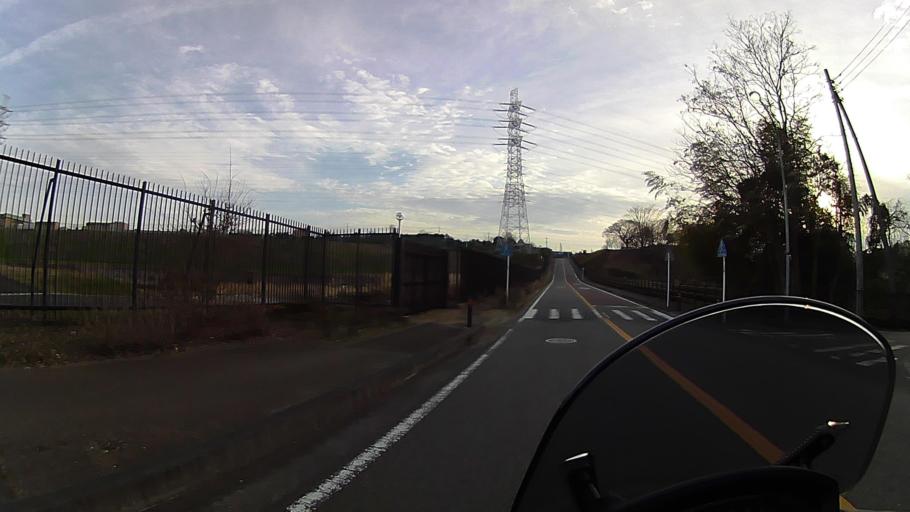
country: JP
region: Kanagawa
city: Atsugi
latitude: 35.4203
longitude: 139.4175
